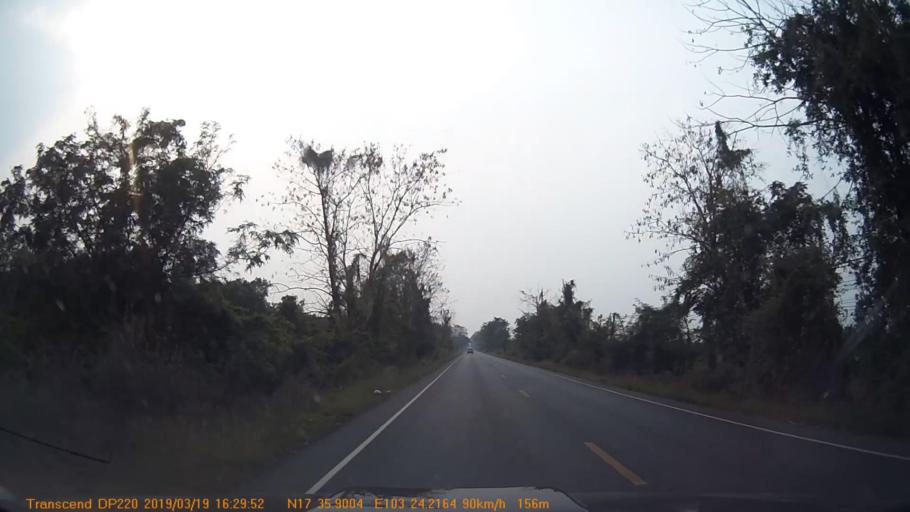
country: TH
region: Sakon Nakhon
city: Sawang Daen Din
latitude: 17.5987
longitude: 103.4030
